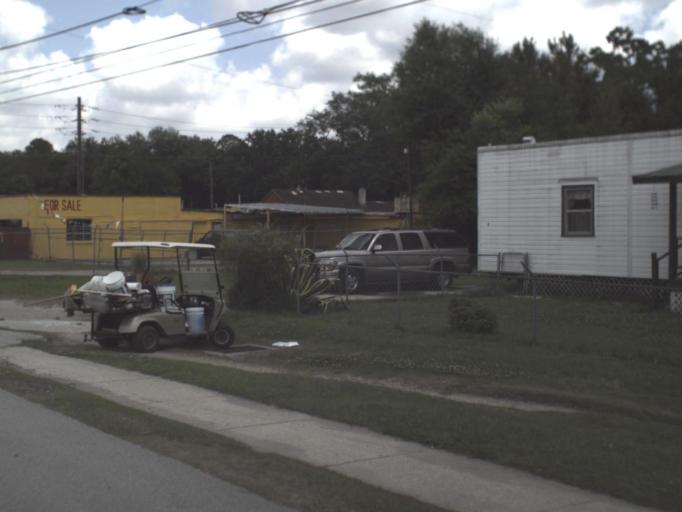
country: US
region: Florida
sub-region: Duval County
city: Jacksonville
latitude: 30.2771
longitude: -81.6260
